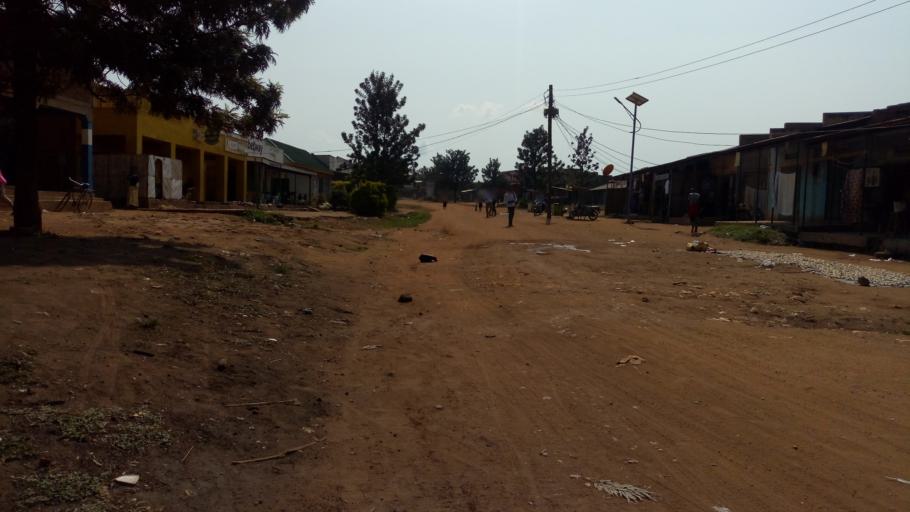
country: UG
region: Western Region
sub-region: Kiryandongo District
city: Kiryandongo
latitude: 1.8107
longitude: 32.0110
